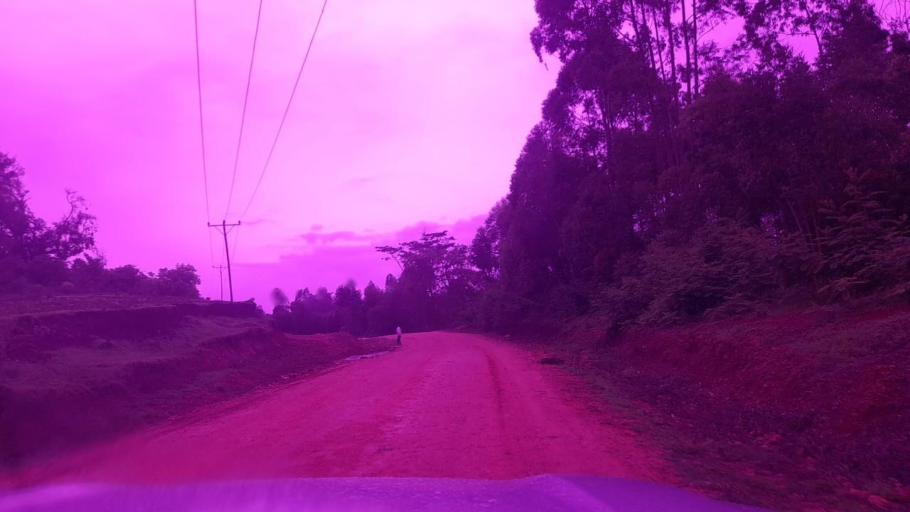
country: ET
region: Southern Nations, Nationalities, and People's Region
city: Bonga
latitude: 7.4427
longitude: 36.1575
